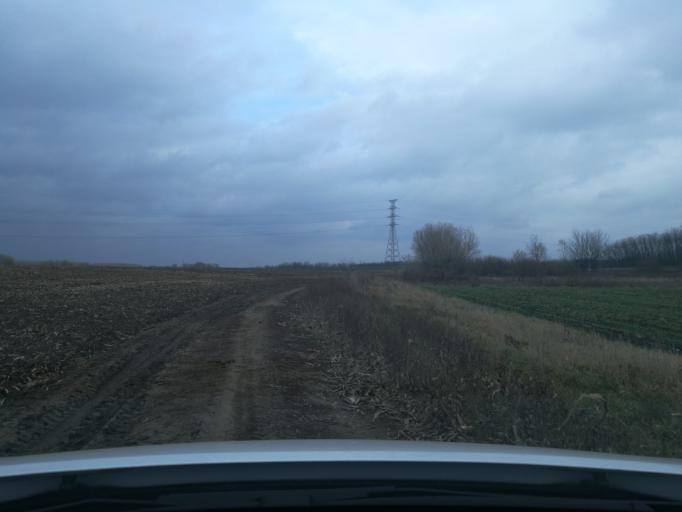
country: HU
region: Szabolcs-Szatmar-Bereg
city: Nyirpazony
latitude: 47.9639
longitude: 21.7842
